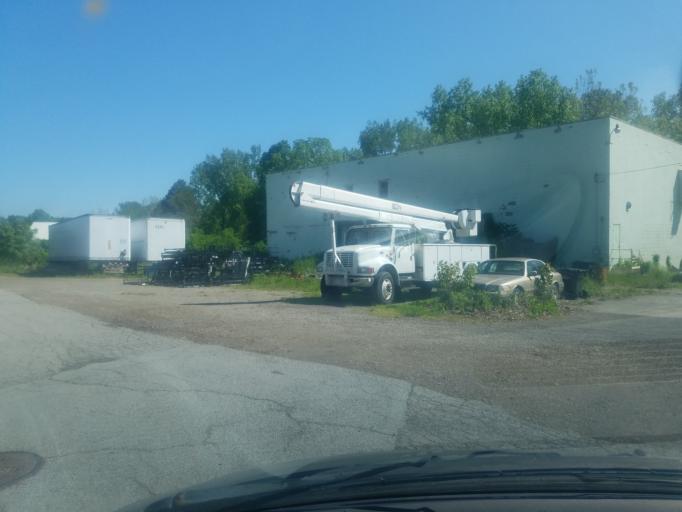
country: US
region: Ohio
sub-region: Huron County
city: Monroeville
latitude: 41.2463
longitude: -82.6936
